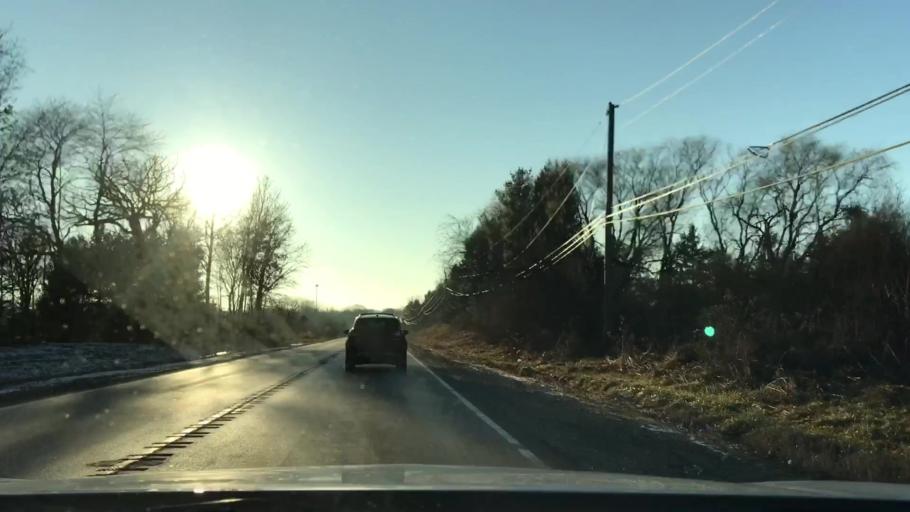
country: US
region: Illinois
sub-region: Kane County
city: Pingree Grove
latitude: 42.0970
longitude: -88.4076
